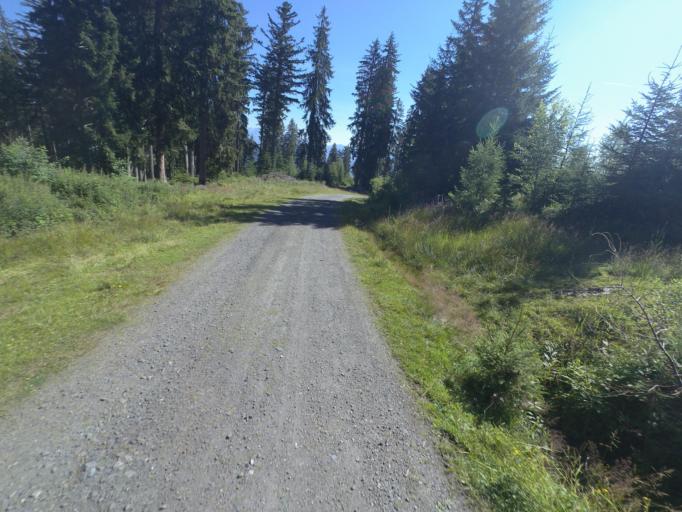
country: AT
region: Salzburg
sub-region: Politischer Bezirk Sankt Johann im Pongau
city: Sankt Veit im Pongau
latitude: 47.3463
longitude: 13.1571
